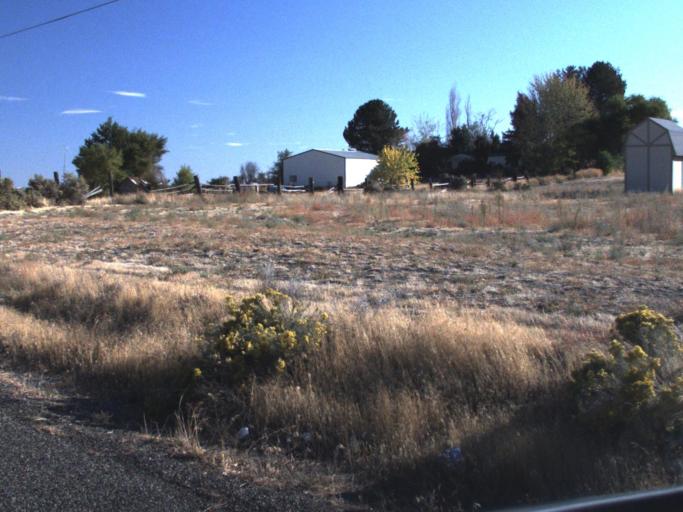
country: US
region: Washington
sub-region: Benton County
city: West Richland
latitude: 46.2971
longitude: -119.3849
